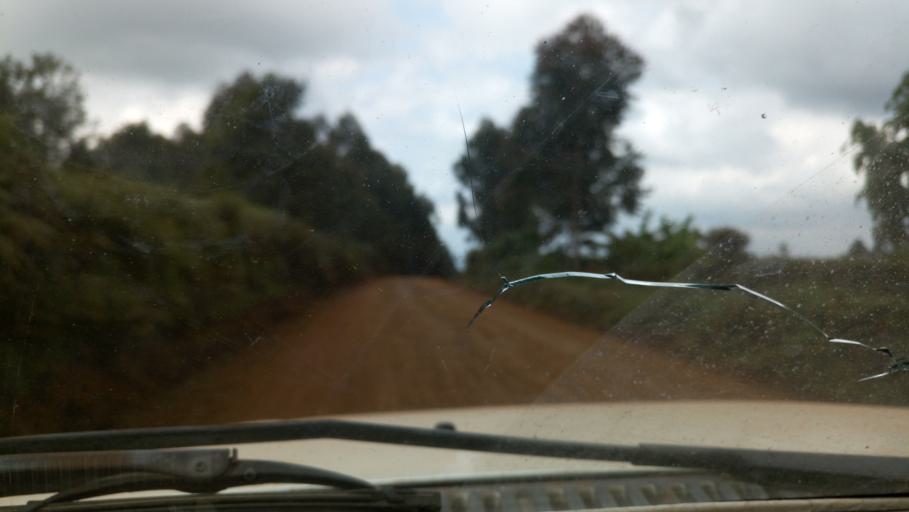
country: KE
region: Murang'a District
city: Kangema
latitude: -0.7645
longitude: 36.9135
